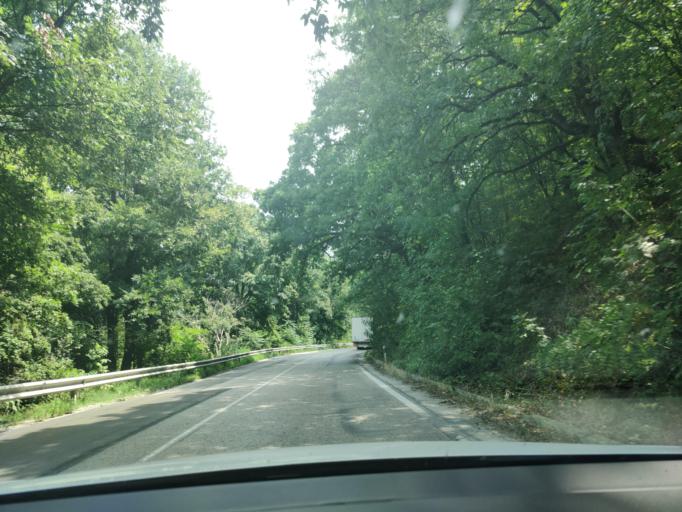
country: BG
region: Vidin
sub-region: Obshtina Dimovo
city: Dimovo
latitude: 43.7358
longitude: 22.7271
